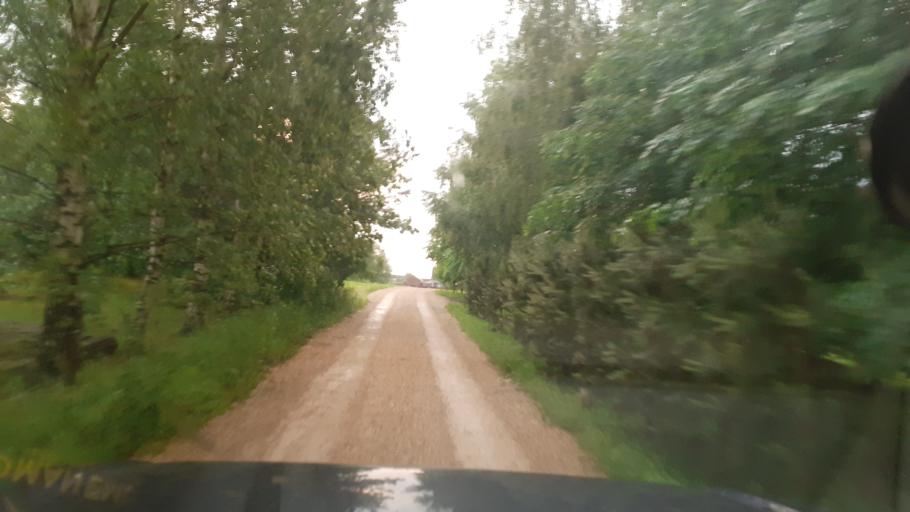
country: RU
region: Moskovskaya
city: Ateptsevo
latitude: 55.3040
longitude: 36.7798
